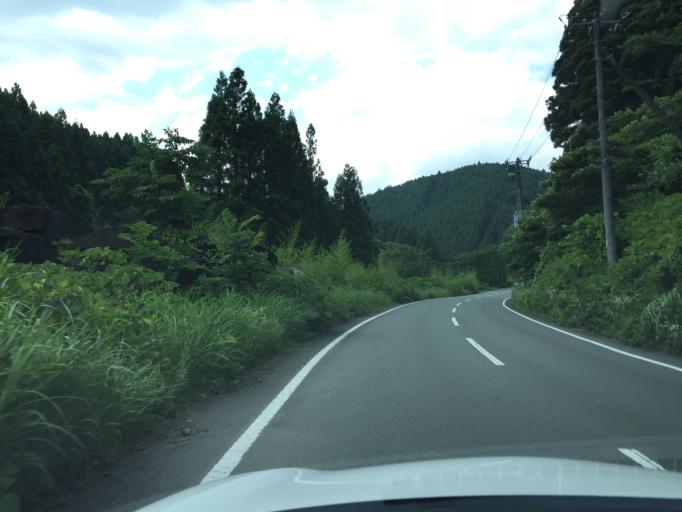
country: JP
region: Fukushima
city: Iwaki
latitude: 37.0049
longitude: 140.7187
